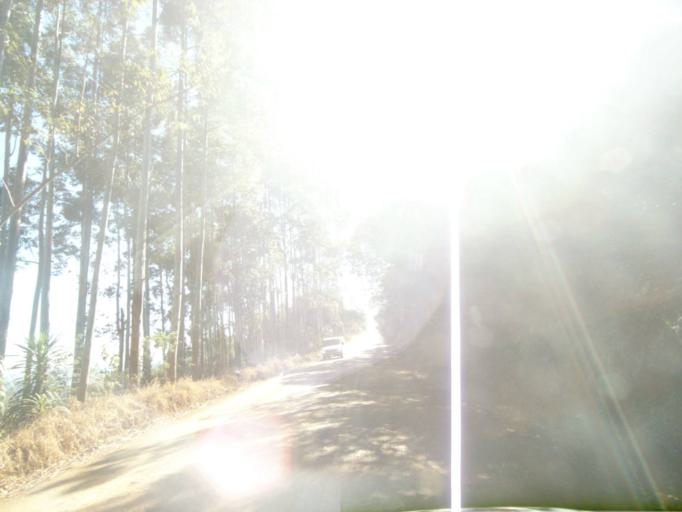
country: BR
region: Parana
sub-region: Tibagi
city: Tibagi
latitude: -24.5922
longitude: -50.6050
